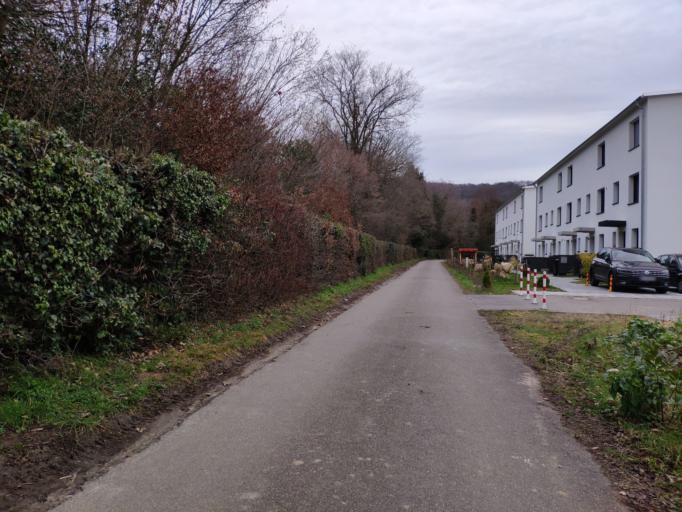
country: CH
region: Basel-Landschaft
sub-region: Bezirk Arlesheim
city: Birsfelden
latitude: 47.5636
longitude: 7.6373
